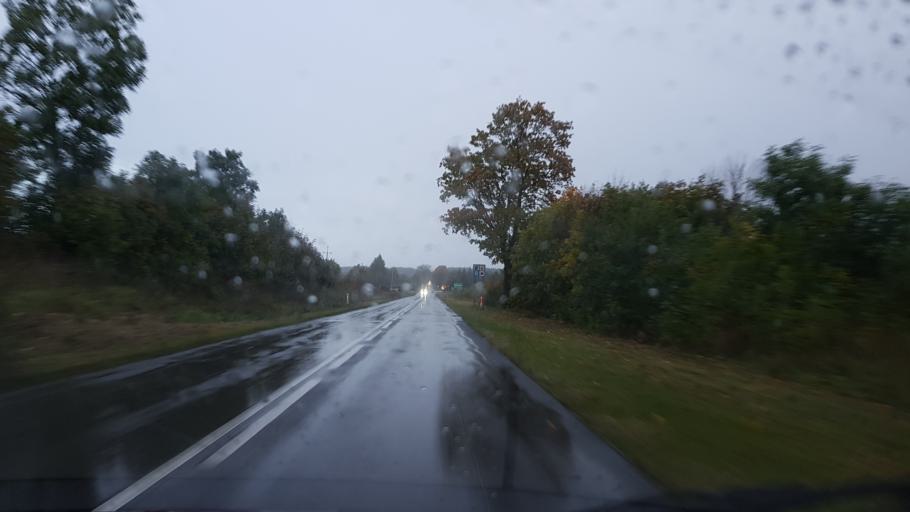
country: PL
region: Greater Poland Voivodeship
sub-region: Powiat pilski
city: Szydlowo
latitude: 53.1585
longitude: 16.6528
